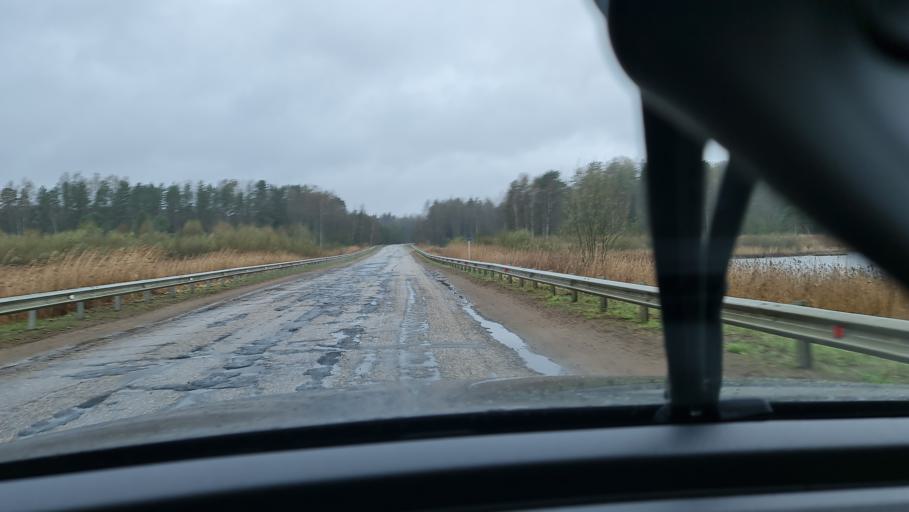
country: RU
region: Novgorod
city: Valday
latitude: 58.0390
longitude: 32.9022
